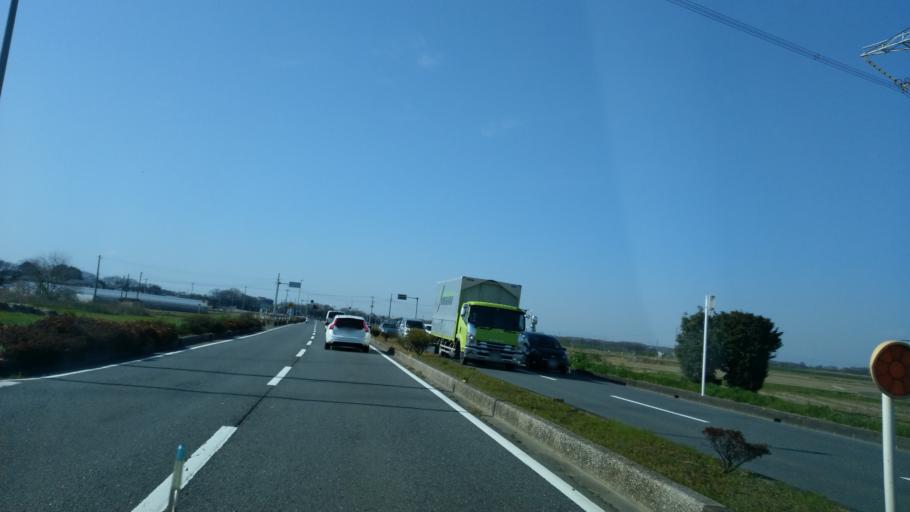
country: JP
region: Saitama
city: Sakado
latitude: 36.0038
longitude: 139.4481
